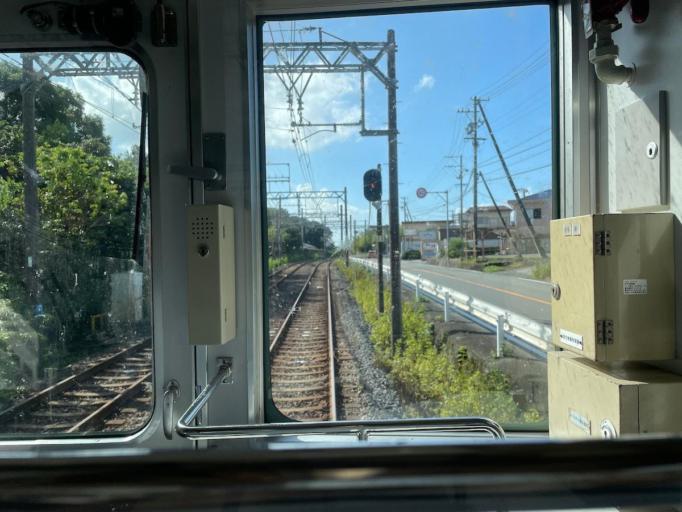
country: JP
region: Mie
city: Toba
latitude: 34.3120
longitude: 136.8254
